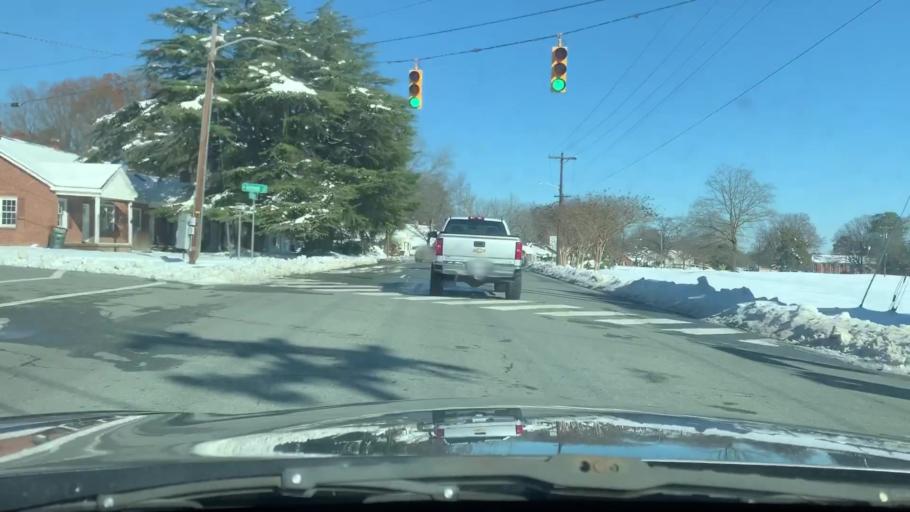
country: US
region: North Carolina
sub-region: Alamance County
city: Burlington
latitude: 36.1010
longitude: -79.4303
